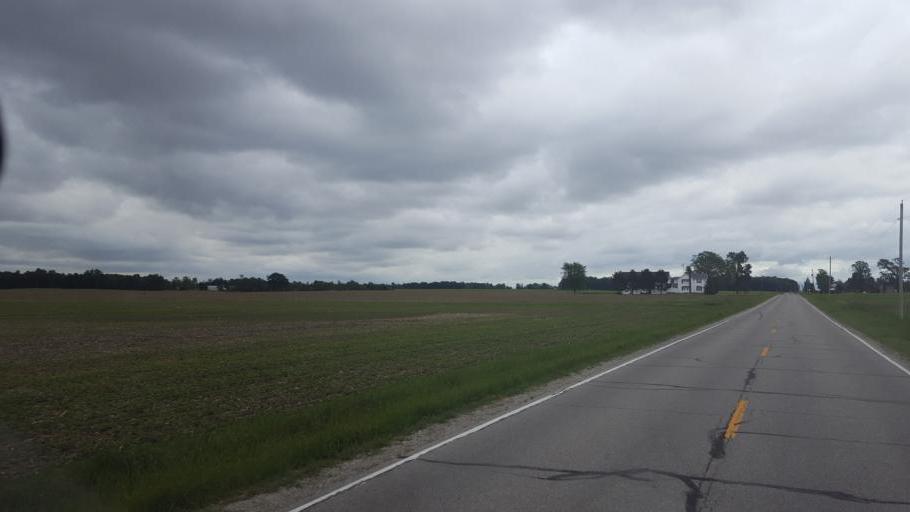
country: US
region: Ohio
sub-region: Crawford County
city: Bucyrus
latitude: 40.7759
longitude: -82.9650
